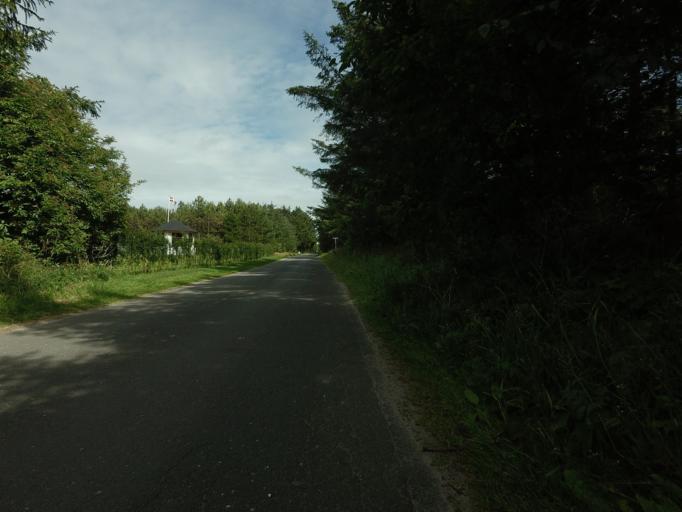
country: DK
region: North Denmark
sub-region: Jammerbugt Kommune
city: Pandrup
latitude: 57.4015
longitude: 9.7466
